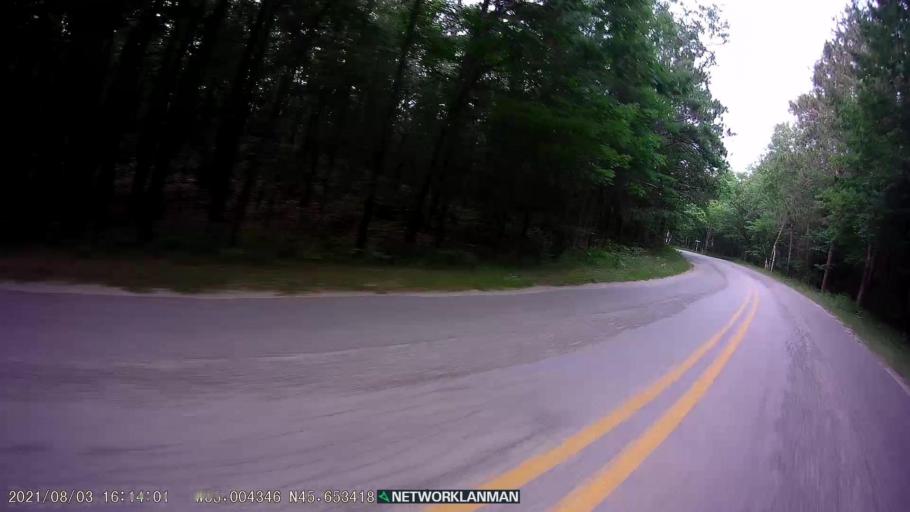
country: US
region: Michigan
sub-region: Emmet County
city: Harbor Springs
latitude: 45.6534
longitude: -85.0036
